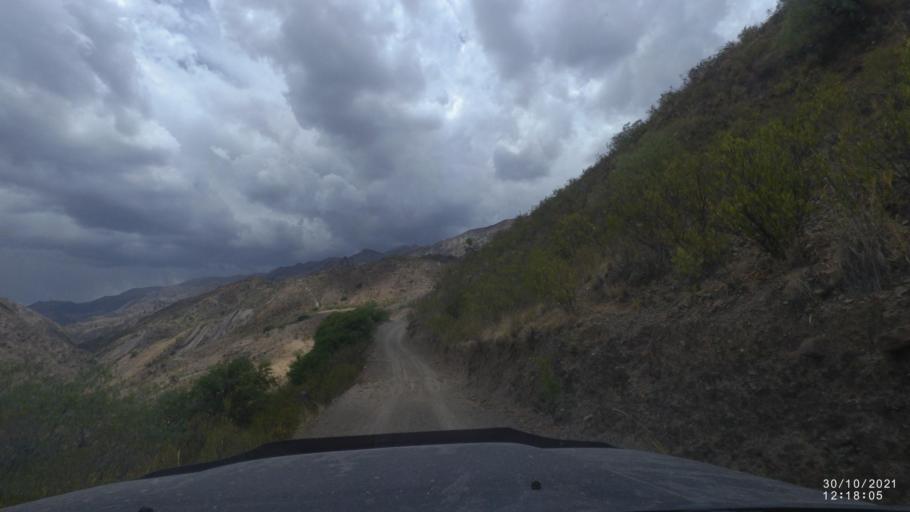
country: BO
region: Cochabamba
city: Colchani
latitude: -17.5667
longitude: -66.6285
